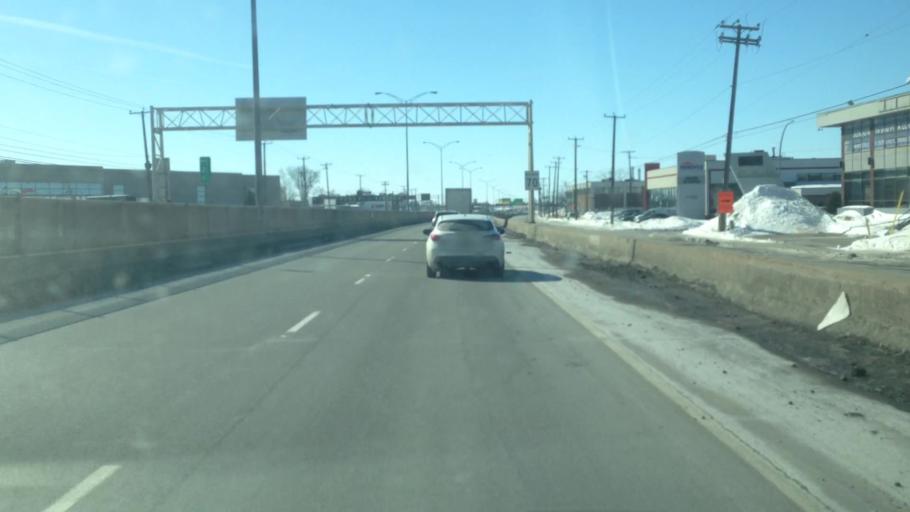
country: CA
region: Quebec
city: Dorval
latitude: 45.4602
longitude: -73.7260
